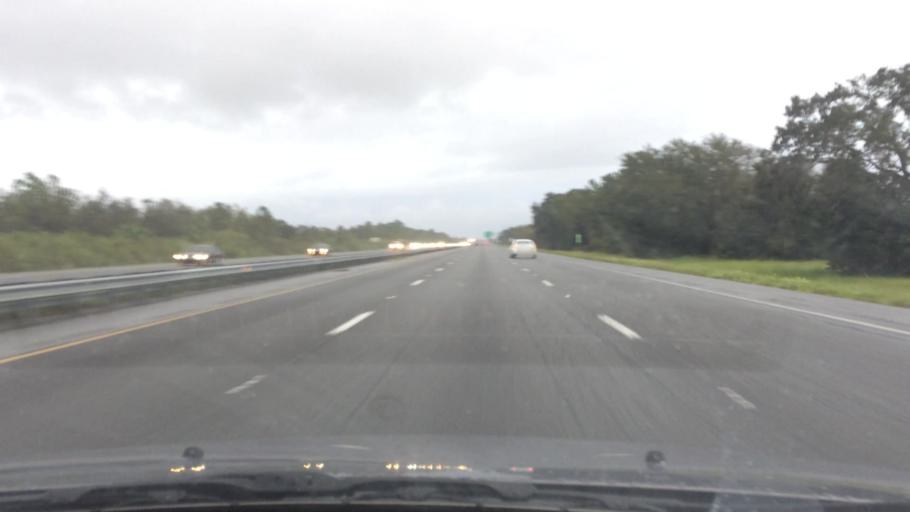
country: US
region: Florida
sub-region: Volusia County
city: Ormond-by-the-Sea
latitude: 29.3181
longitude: -81.1314
